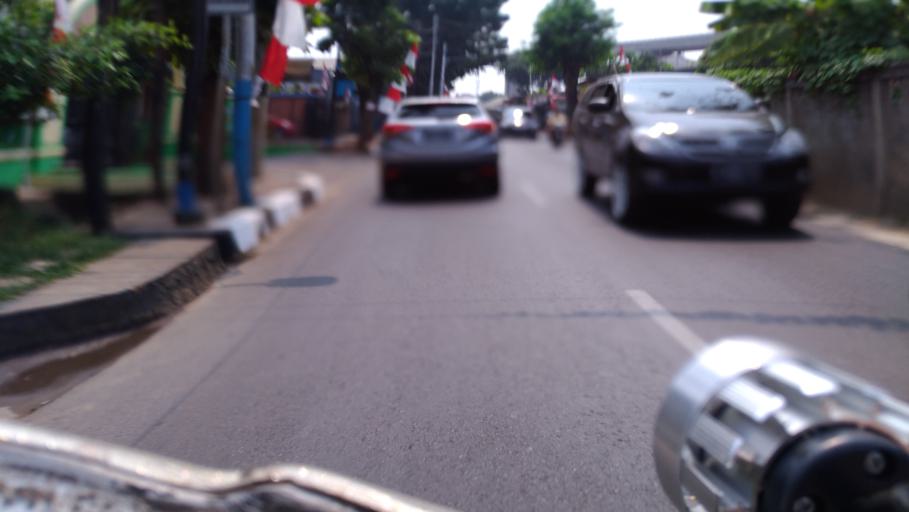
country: ID
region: West Java
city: Cileungsir
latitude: -6.3400
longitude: 106.8877
